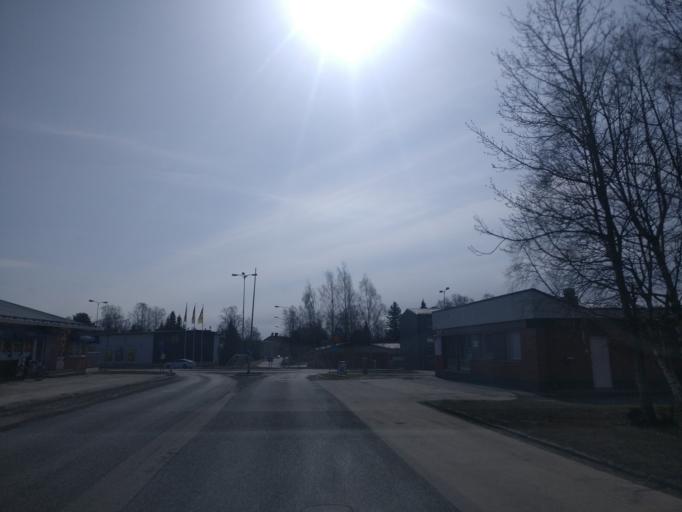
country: FI
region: Lapland
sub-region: Kemi-Tornio
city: Kemi
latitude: 65.7305
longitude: 24.5990
